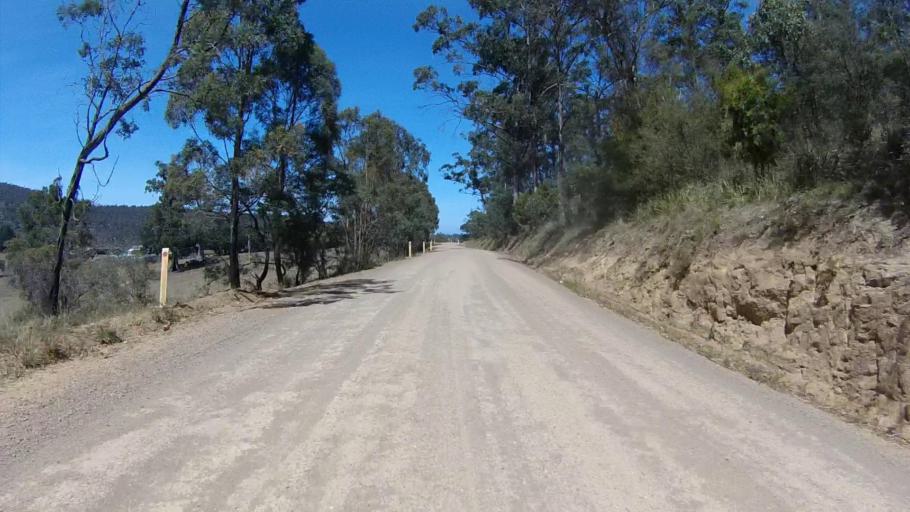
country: AU
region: Tasmania
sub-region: Sorell
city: Sorell
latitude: -42.7565
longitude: 147.6827
